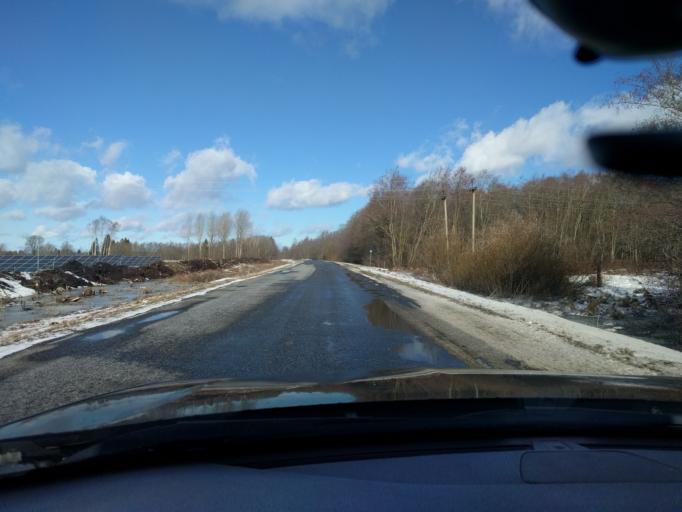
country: EE
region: Harju
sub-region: Raasiku vald
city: Raasiku
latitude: 59.3020
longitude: 25.1720
